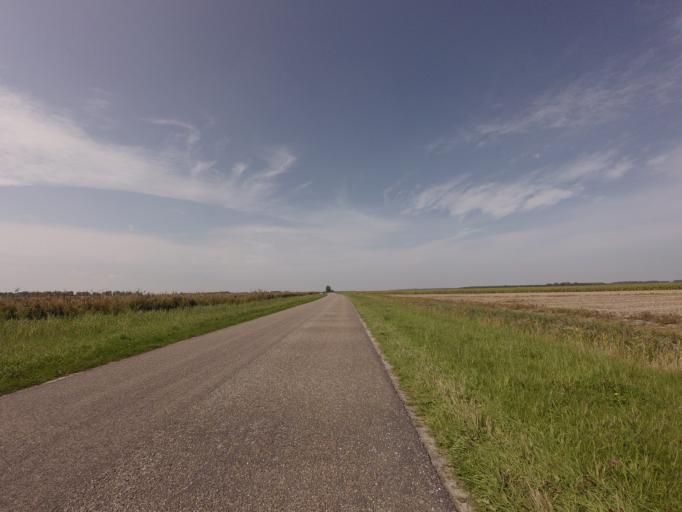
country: NL
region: Groningen
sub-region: Gemeente De Marne
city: Ulrum
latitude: 53.3447
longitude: 6.2778
